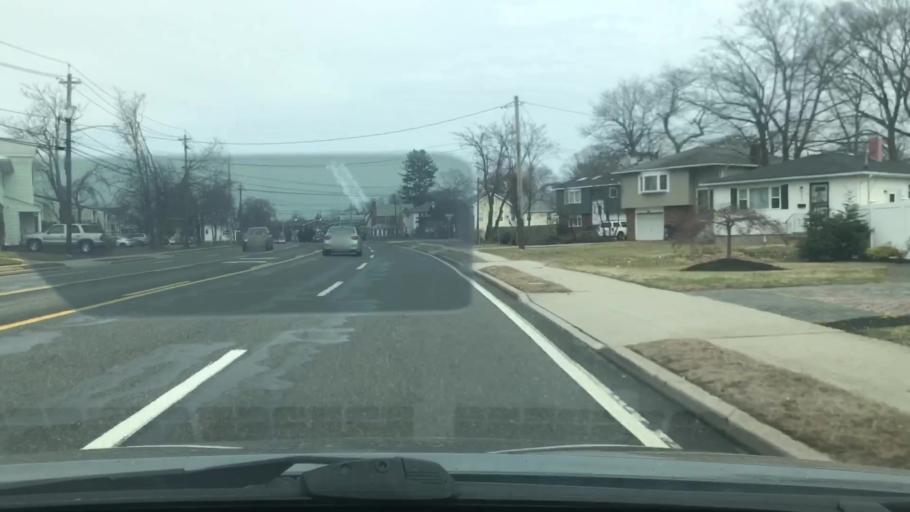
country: US
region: New York
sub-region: Suffolk County
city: Babylon
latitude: 40.6974
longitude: -73.3430
